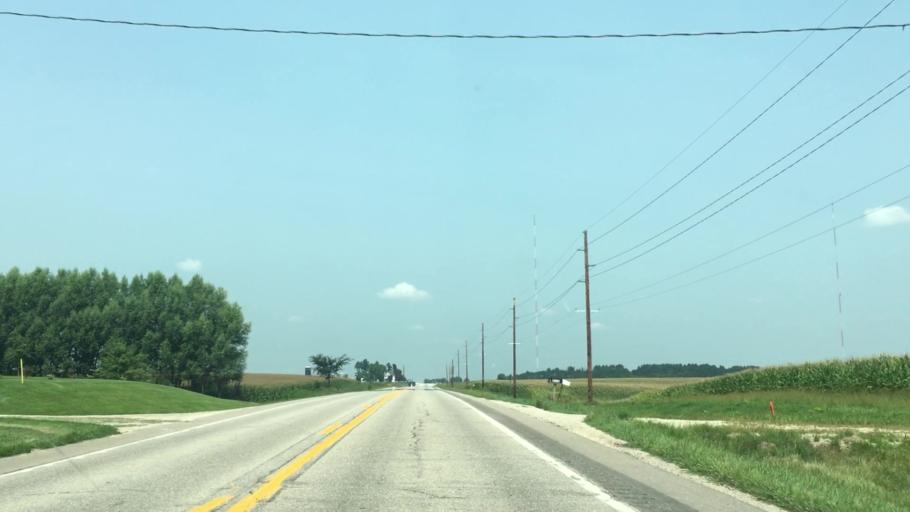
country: US
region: Iowa
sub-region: Benton County
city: Urbana
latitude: 42.2754
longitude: -91.8903
